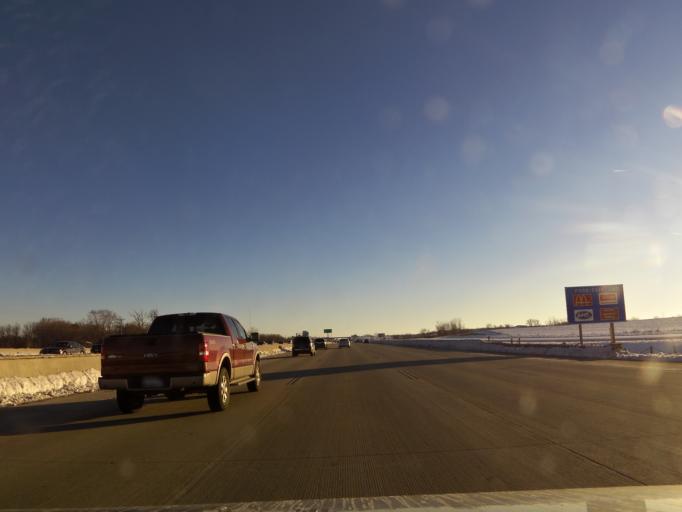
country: US
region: Wisconsin
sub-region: Kenosha County
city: Pleasant Prairie
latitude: 42.5358
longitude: -87.9525
